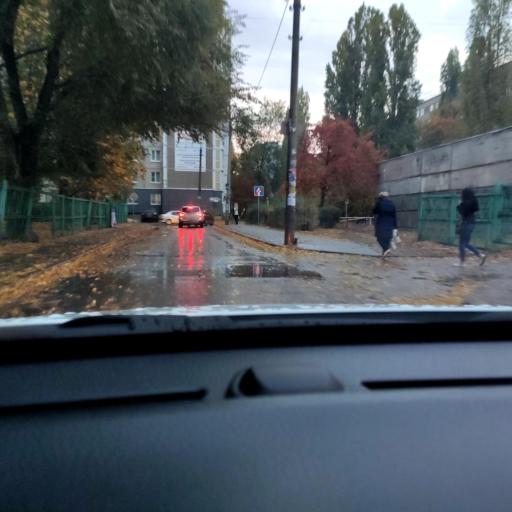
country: RU
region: Voronezj
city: Podgornoye
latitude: 51.7098
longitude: 39.1681
